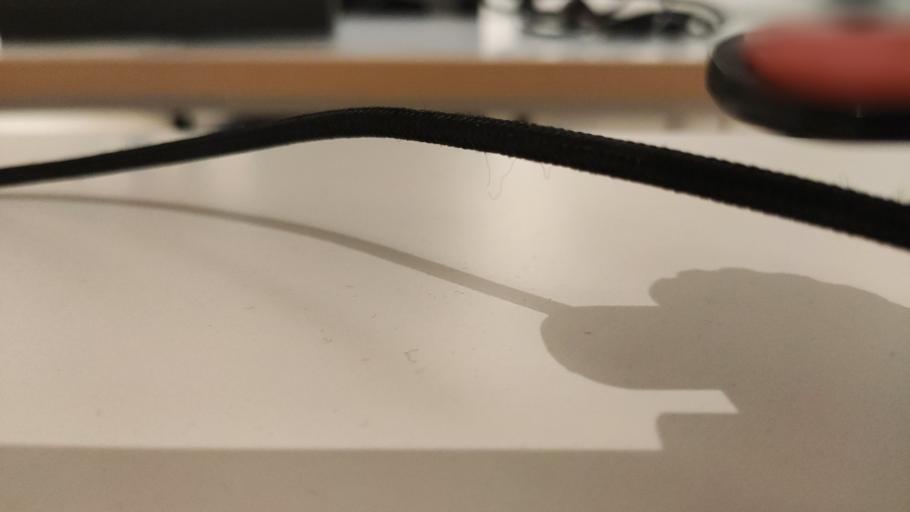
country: RU
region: Moskovskaya
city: Dorokhovo
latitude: 55.5258
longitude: 36.3551
